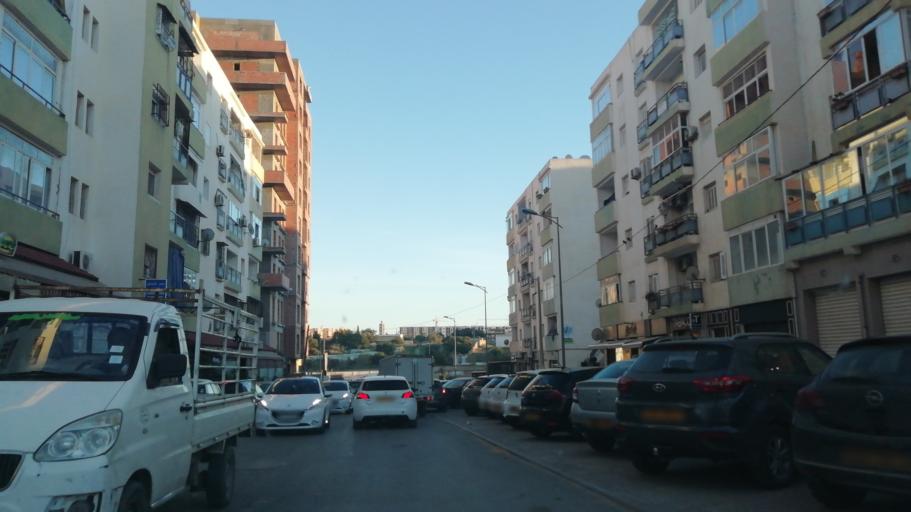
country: DZ
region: Oran
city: Bir el Djir
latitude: 35.7168
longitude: -0.5751
